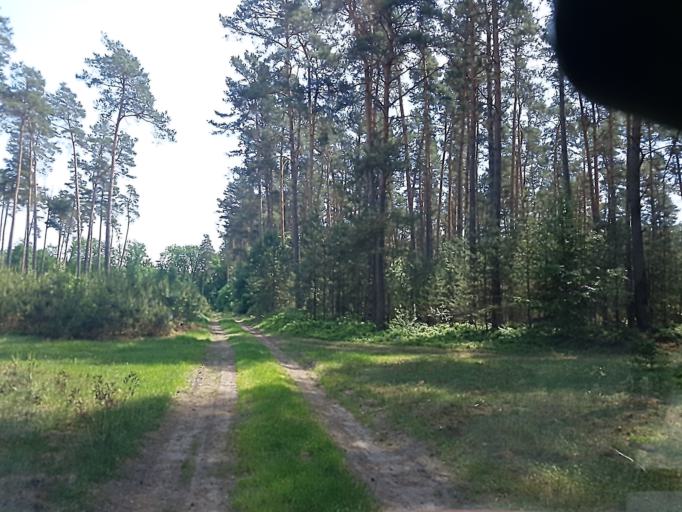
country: DE
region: Brandenburg
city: Gorzke
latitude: 52.1004
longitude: 12.3014
